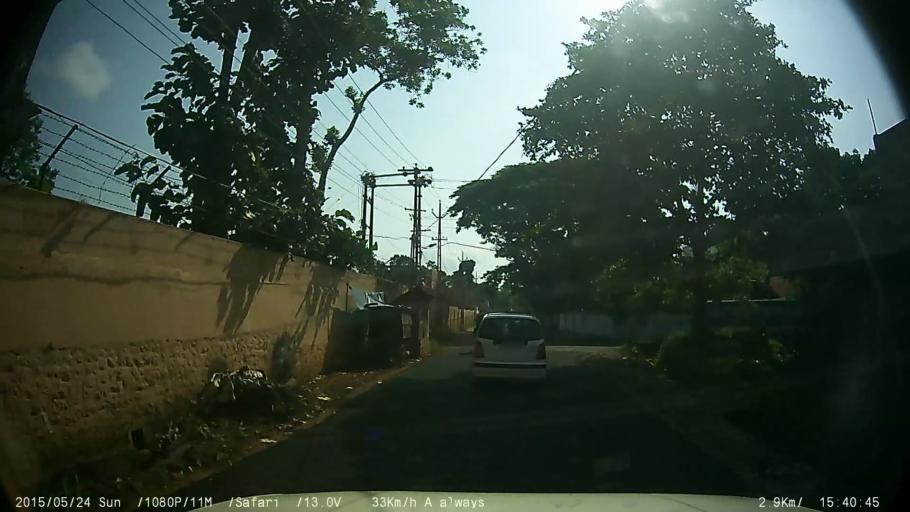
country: IN
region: Kerala
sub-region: Kottayam
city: Changanacheri
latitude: 9.4415
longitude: 76.5457
